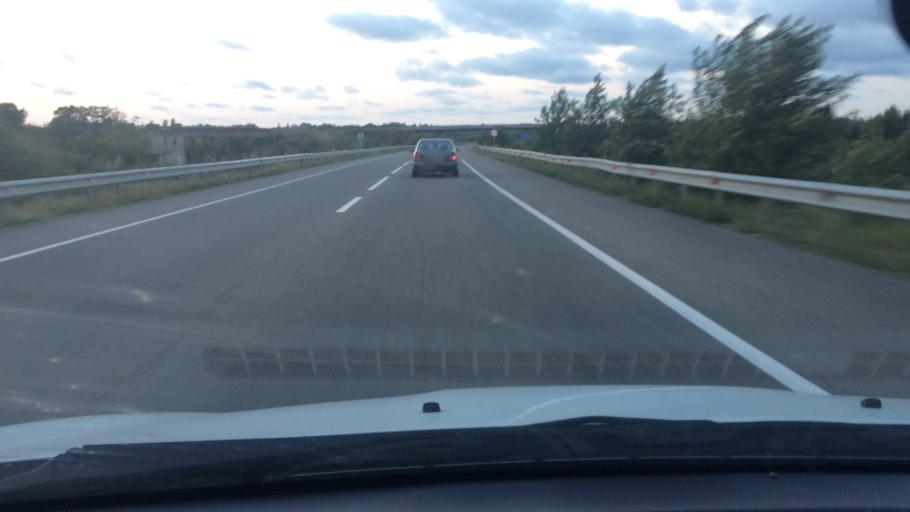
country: GE
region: Guria
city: Urek'i
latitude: 41.9149
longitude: 41.7780
